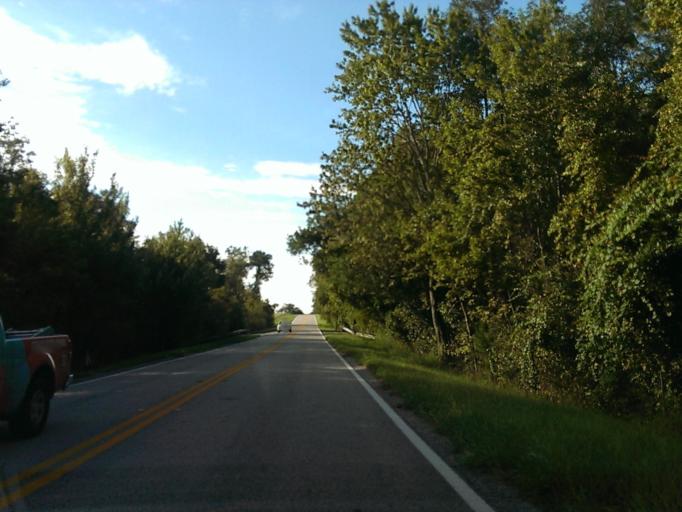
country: US
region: Florida
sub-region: Polk County
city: Citrus Ridge
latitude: 28.3986
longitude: -81.6376
